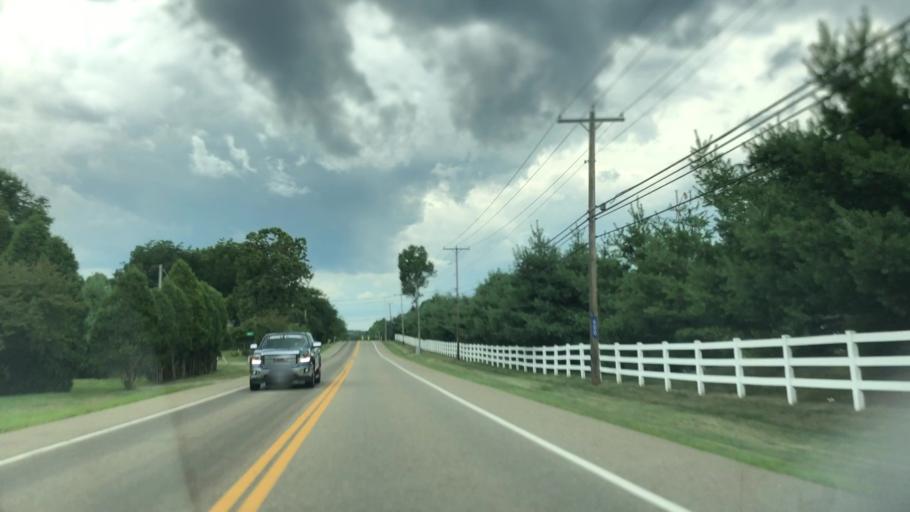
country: US
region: Ohio
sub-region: Summit County
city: Green
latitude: 40.9533
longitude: -81.5100
